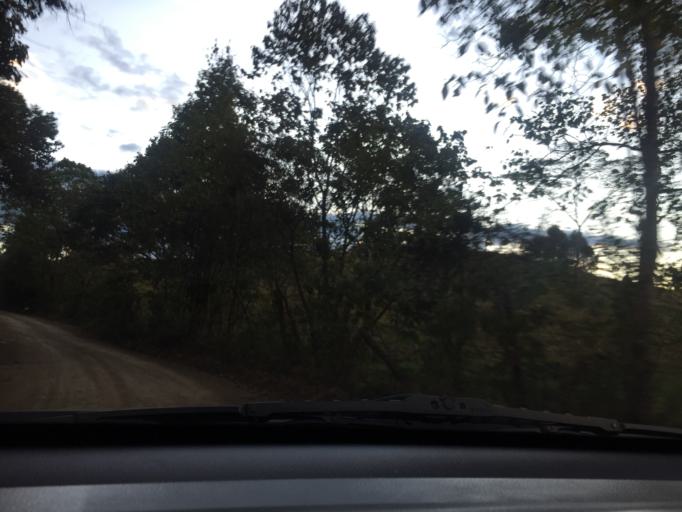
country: CO
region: Cundinamarca
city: Zipacon
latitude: 4.7043
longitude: -74.4081
